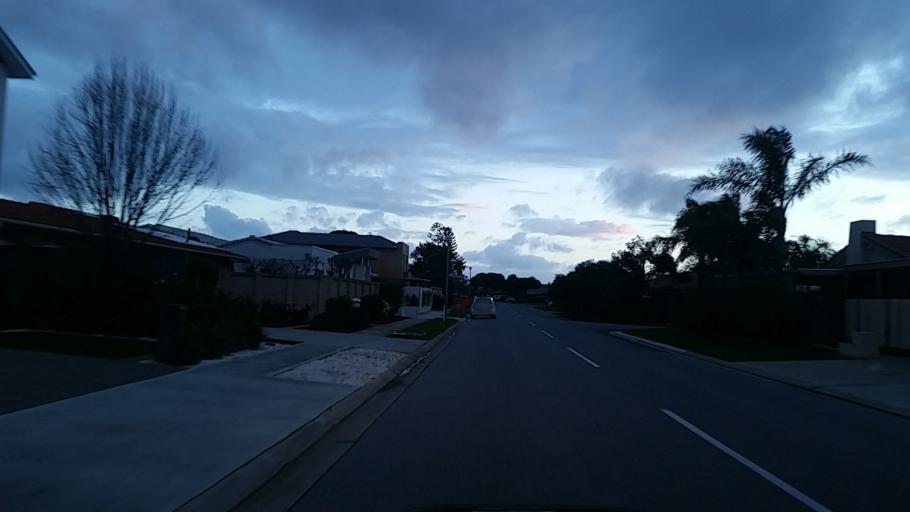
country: AU
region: South Australia
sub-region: Charles Sturt
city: West Lakes Shore
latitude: -34.8673
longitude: 138.4877
